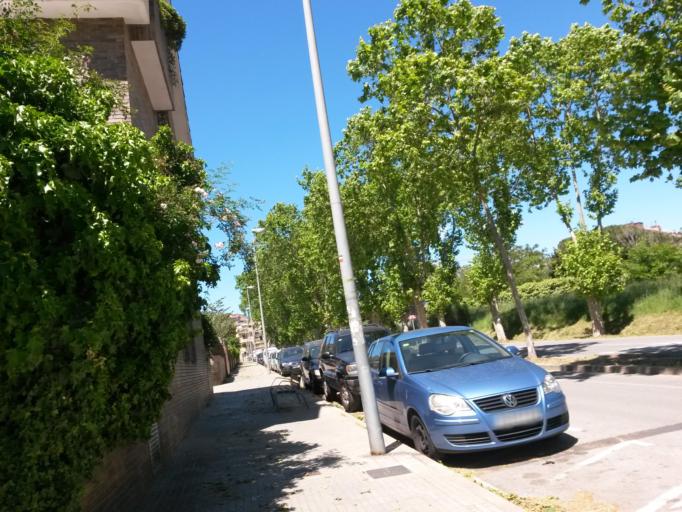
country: ES
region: Catalonia
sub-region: Provincia de Barcelona
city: Cerdanyola del Valles
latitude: 41.4870
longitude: 2.1321
